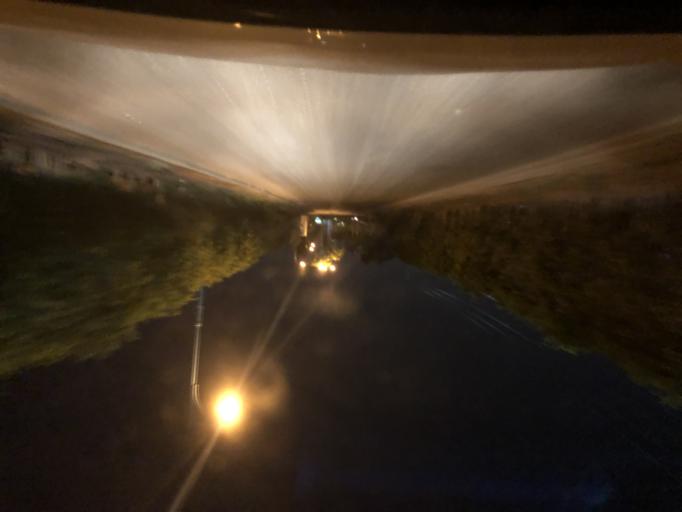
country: IL
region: Central District
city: Jaljulya
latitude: 32.1693
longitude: 34.9454
